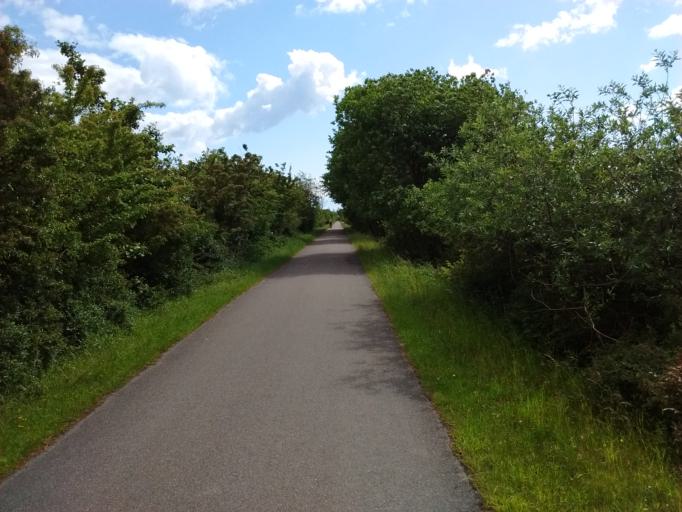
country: DK
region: Capital Region
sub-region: Tarnby Kommune
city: Tarnby
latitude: 55.6096
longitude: 12.5768
